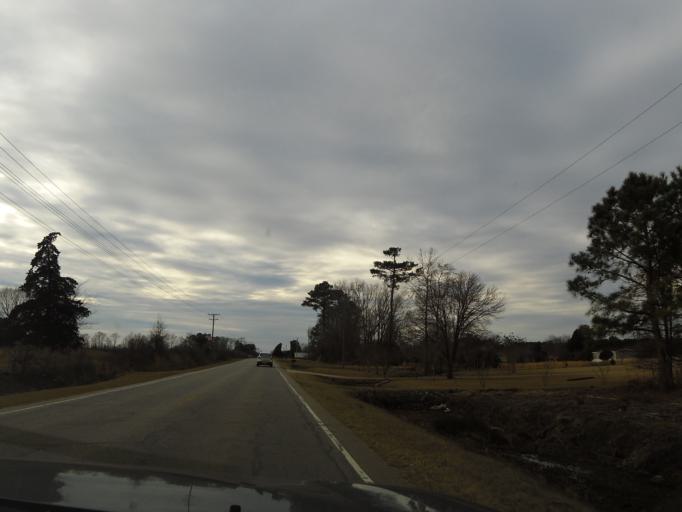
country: US
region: North Carolina
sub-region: Nash County
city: Rocky Mount
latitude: 35.9660
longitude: -77.6815
